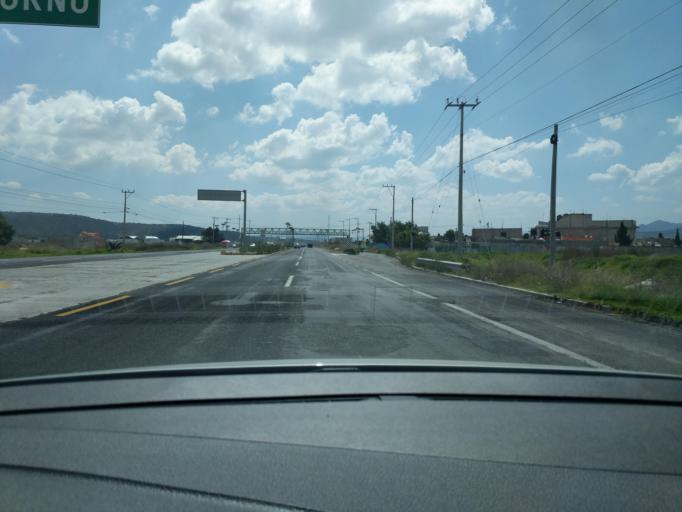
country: MX
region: Hidalgo
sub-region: Mineral de la Reforma
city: Rinconada de los Angeles
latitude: 20.0184
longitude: -98.7211
